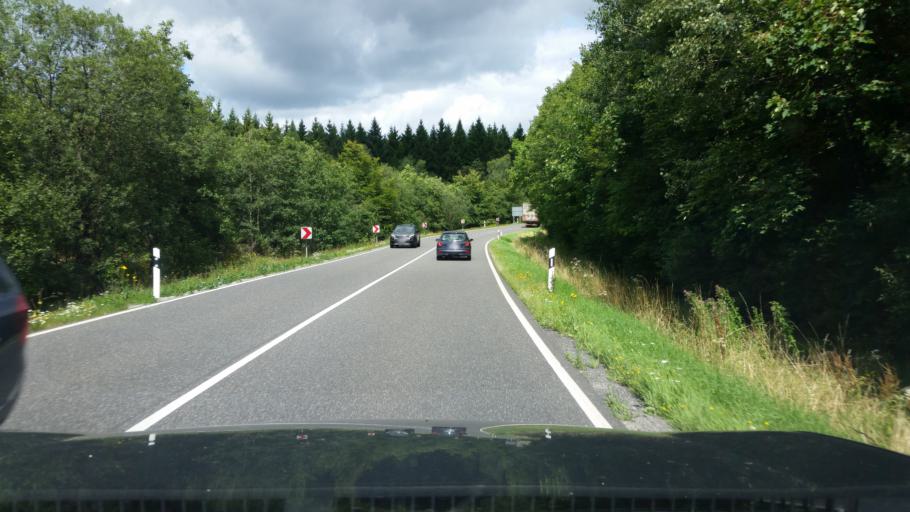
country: DE
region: North Rhine-Westphalia
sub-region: Regierungsbezirk Koln
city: Blankenheim
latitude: 50.4512
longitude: 6.7055
